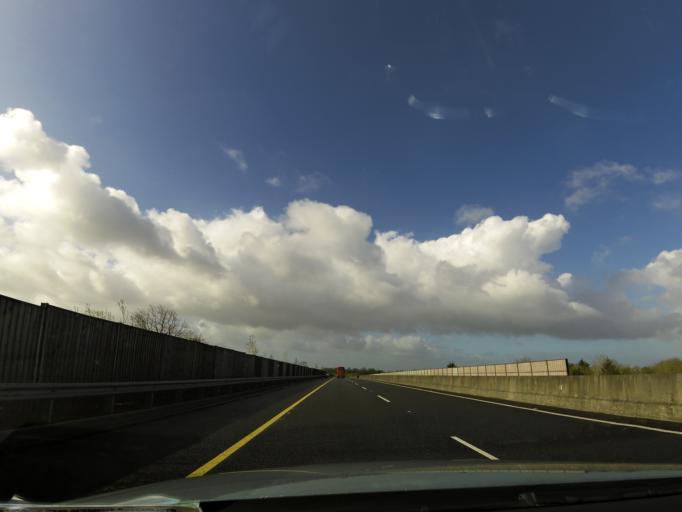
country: IE
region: Munster
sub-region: County Limerick
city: Castleconnell
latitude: 52.7063
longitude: -8.4830
